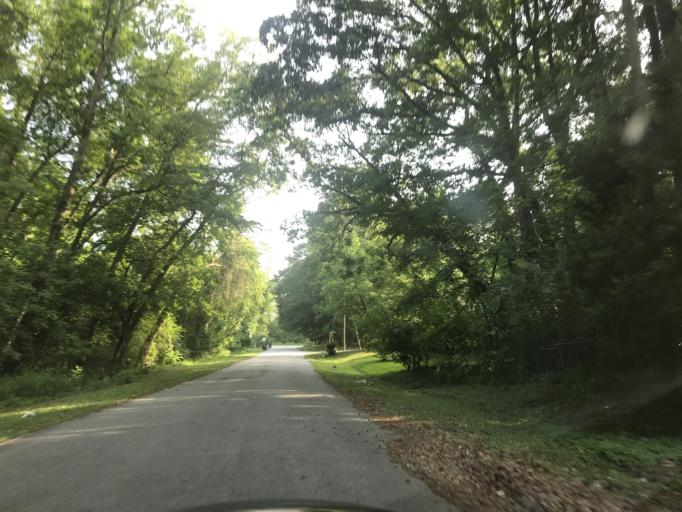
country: US
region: North Carolina
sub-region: Wake County
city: Garner
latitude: 35.7428
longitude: -78.5709
